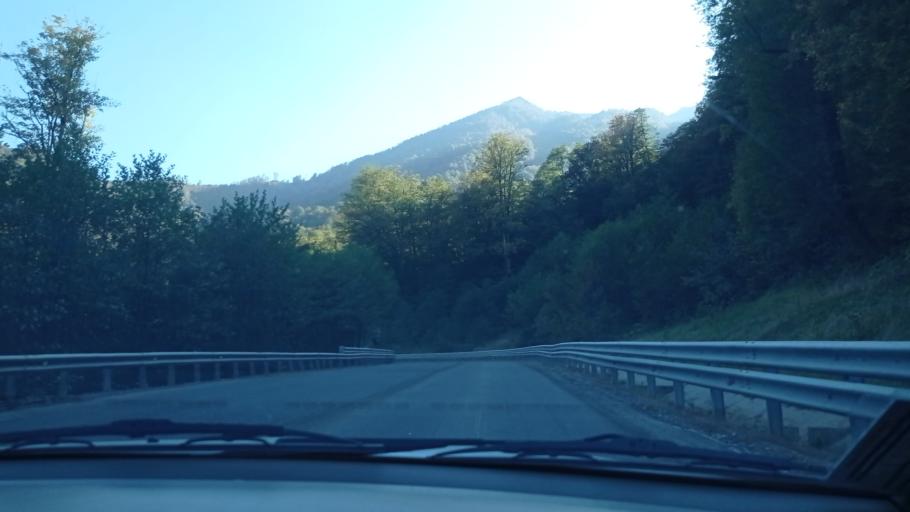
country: RU
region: Krasnodarskiy
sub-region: Sochi City
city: Krasnaya Polyana
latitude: 43.6604
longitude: 40.3000
